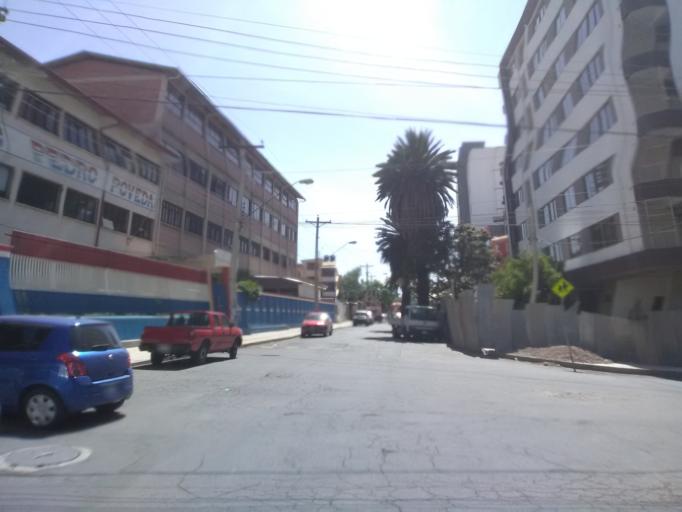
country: BO
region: Cochabamba
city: Cochabamba
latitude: -17.3749
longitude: -66.1442
